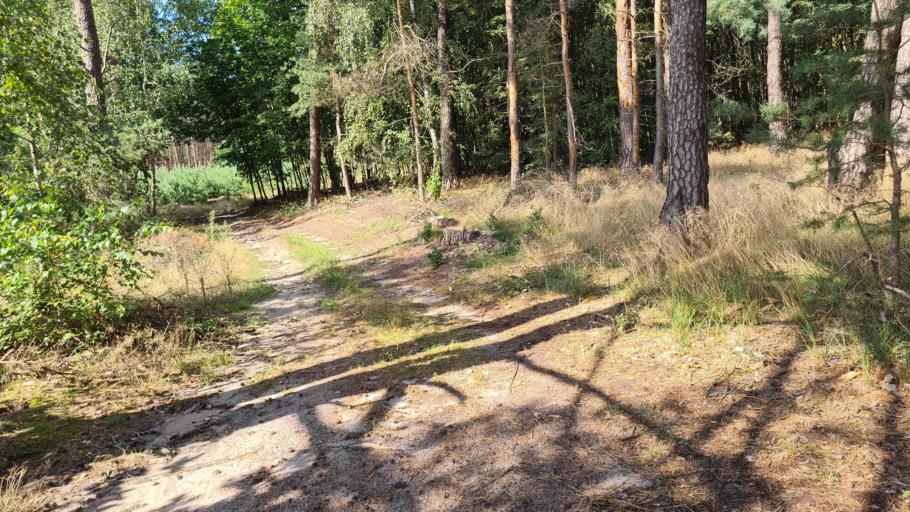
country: DE
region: Brandenburg
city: Crinitz
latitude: 51.7095
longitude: 13.7230
